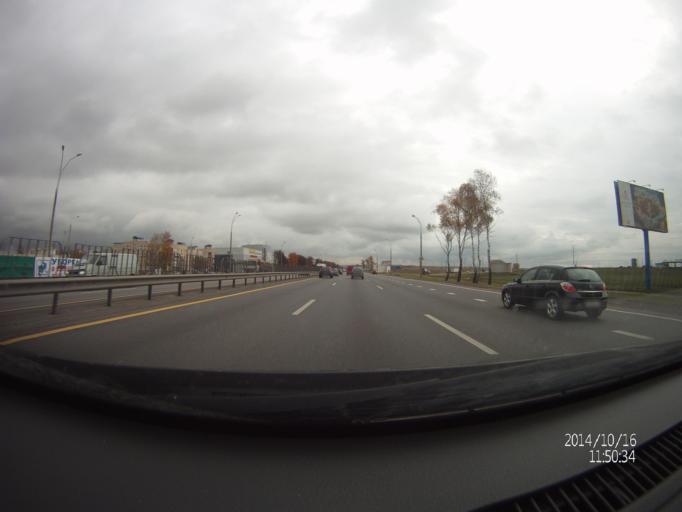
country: BY
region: Minsk
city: Machulishchy
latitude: 53.8333
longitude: 27.6048
